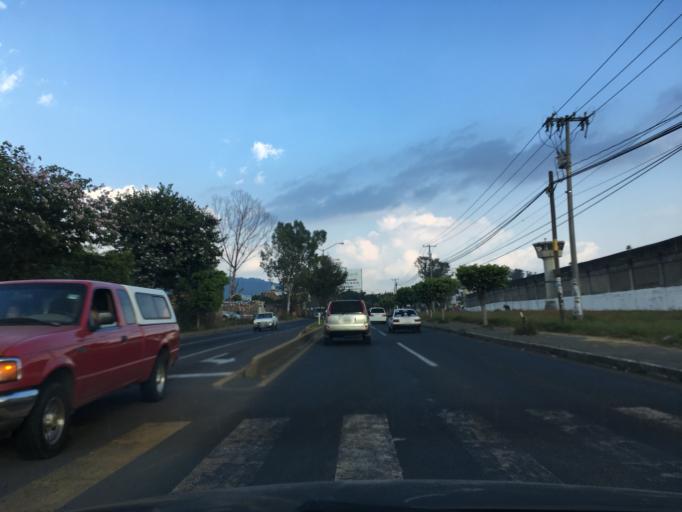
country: MX
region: Michoacan
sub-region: Uruapan
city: Toreo Bajo (El Toreo Bajo)
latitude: 19.4243
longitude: -102.0145
